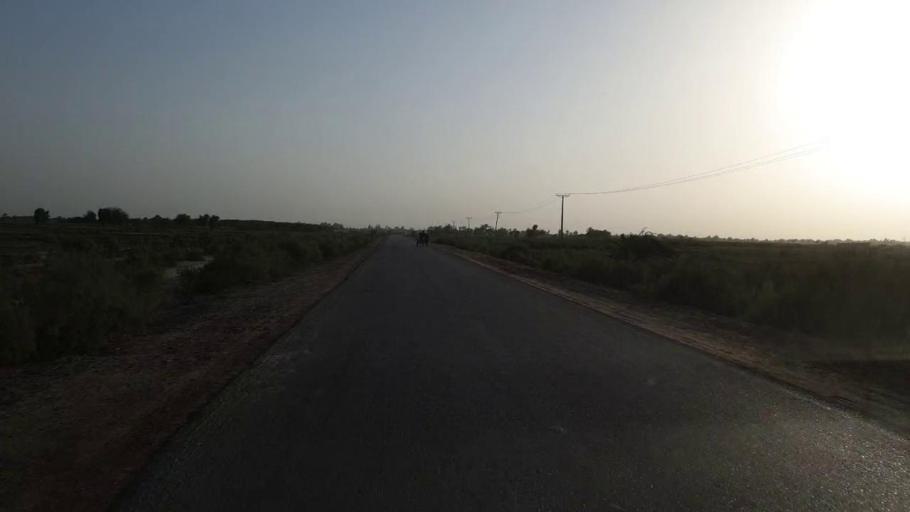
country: PK
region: Sindh
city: Jam Sahib
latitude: 26.2806
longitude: 68.5765
